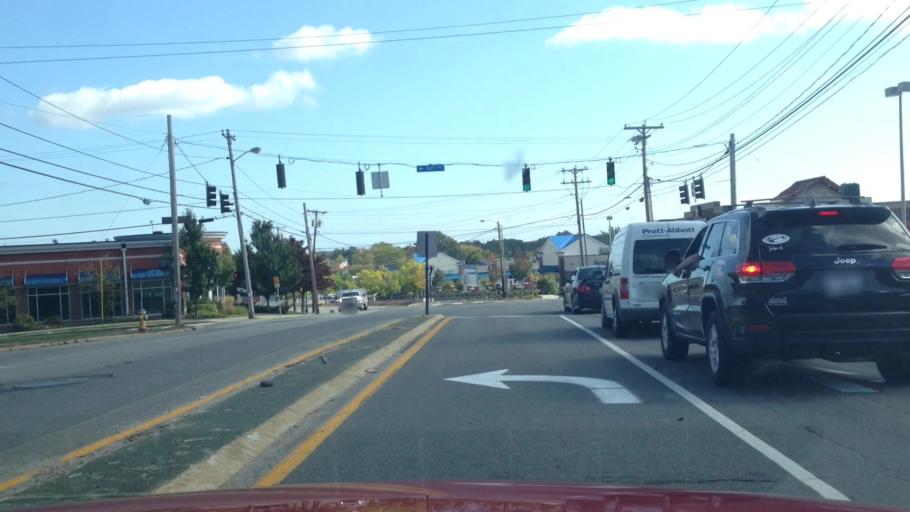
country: US
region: Maine
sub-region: Cumberland County
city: South Portland Gardens
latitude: 43.6752
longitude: -70.3241
